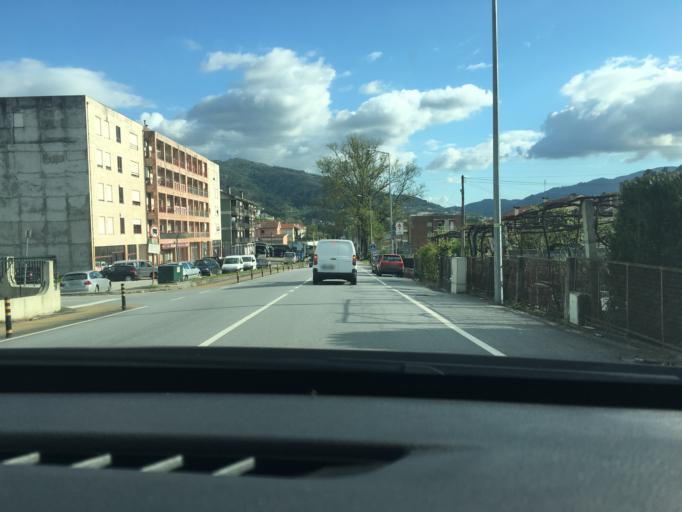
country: PT
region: Viana do Castelo
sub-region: Ponte da Barca
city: Ponte da Barca
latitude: 41.7980
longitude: -8.4146
